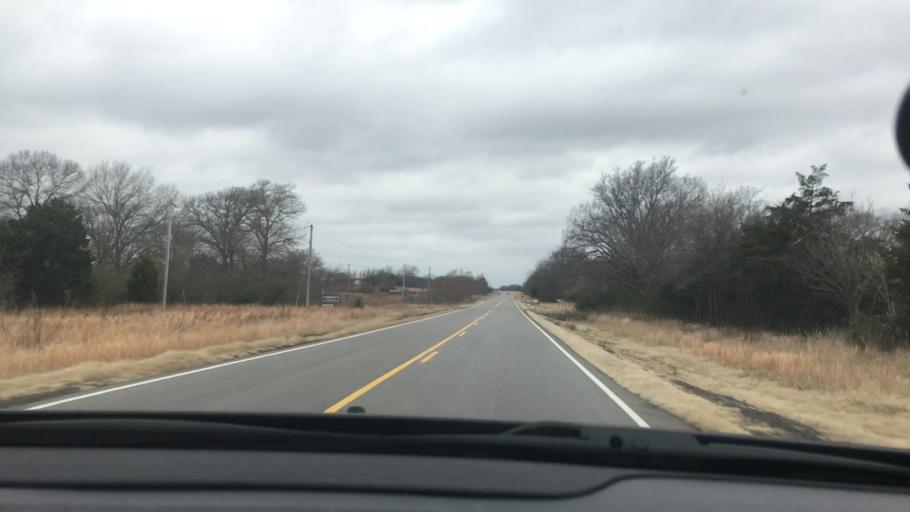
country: US
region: Oklahoma
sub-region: Atoka County
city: Atoka
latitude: 34.3749
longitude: -96.1617
